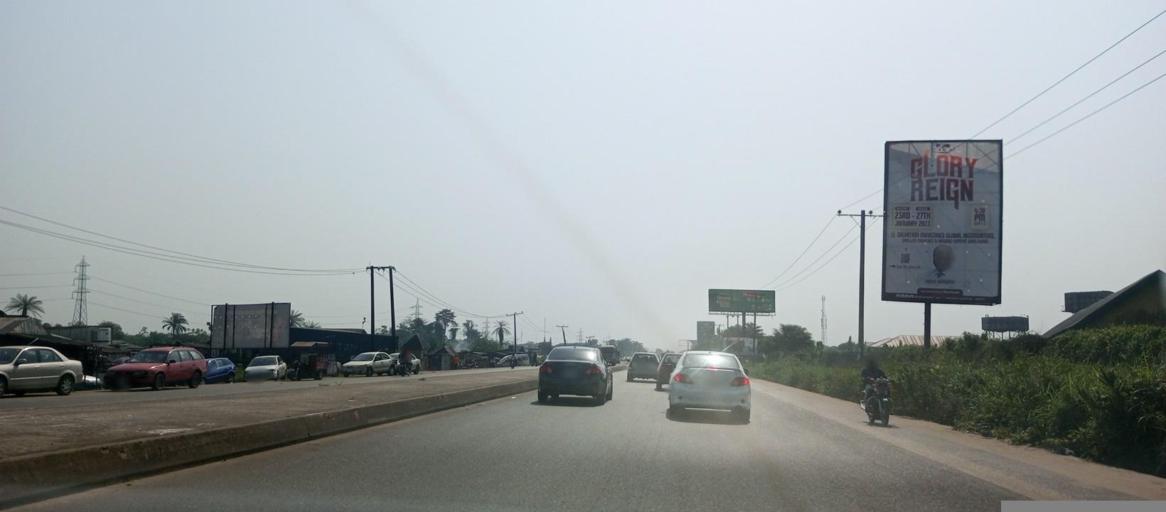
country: NG
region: Rivers
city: Emuoha
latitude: 4.8970
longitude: 6.9094
